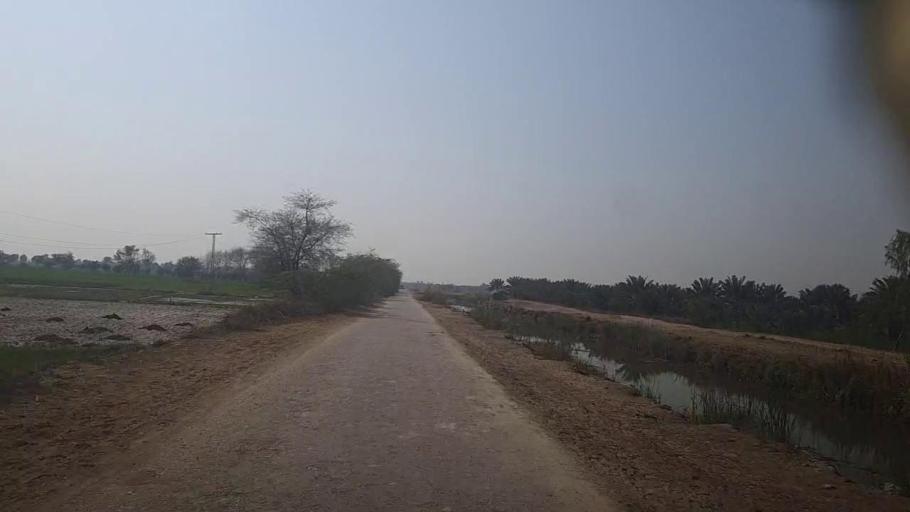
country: PK
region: Sindh
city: Kot Diji
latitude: 27.4079
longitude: 68.7861
